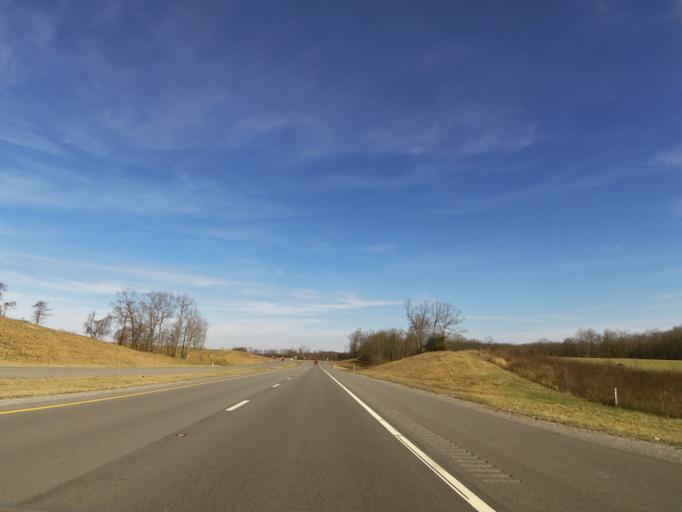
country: US
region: Tennessee
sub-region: Warren County
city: McMinnville
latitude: 35.7244
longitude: -85.8918
